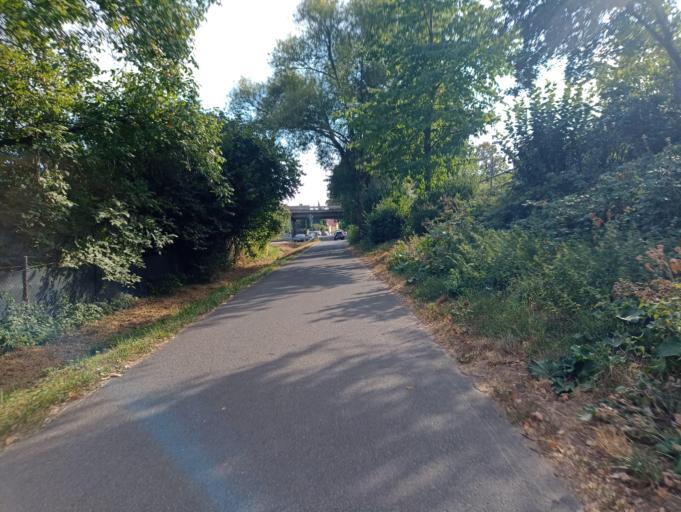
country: DE
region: Hesse
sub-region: Regierungsbezirk Darmstadt
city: Bad Homburg vor der Hoehe
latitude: 50.1926
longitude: 8.6364
